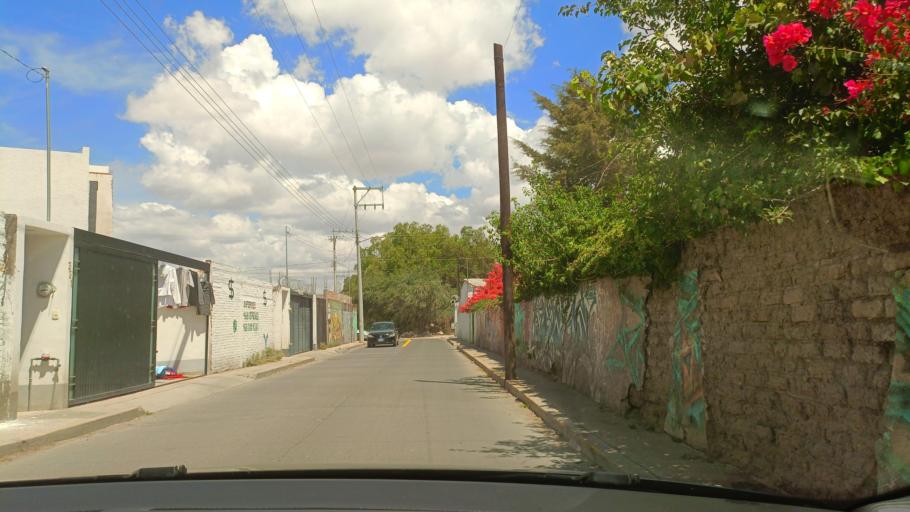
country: MX
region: Guanajuato
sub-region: San Luis de la Paz
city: San Luis de la Paz
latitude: 21.3046
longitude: -100.5206
